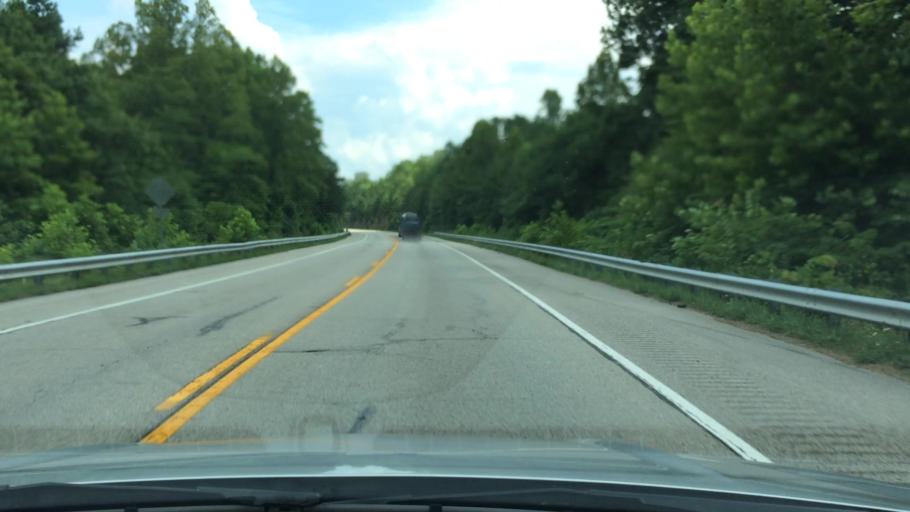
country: US
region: Kentucky
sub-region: McCreary County
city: Whitley City
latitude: 36.9152
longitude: -84.5155
